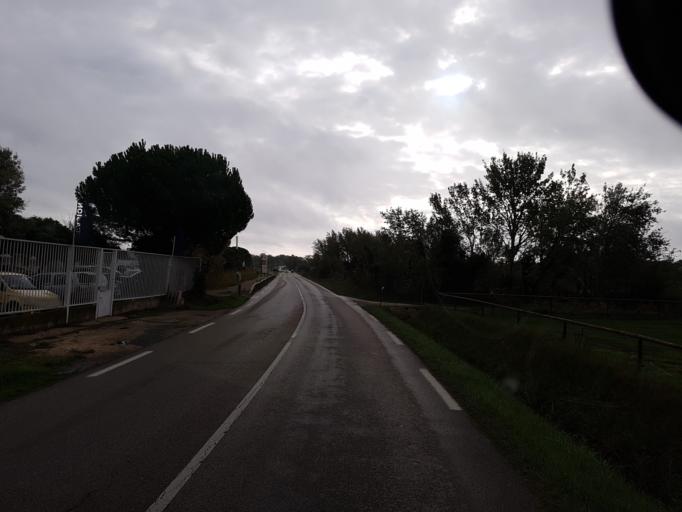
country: FR
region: Languedoc-Roussillon
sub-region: Departement du Gard
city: Saint-Gilles
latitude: 43.6701
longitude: 4.4435
